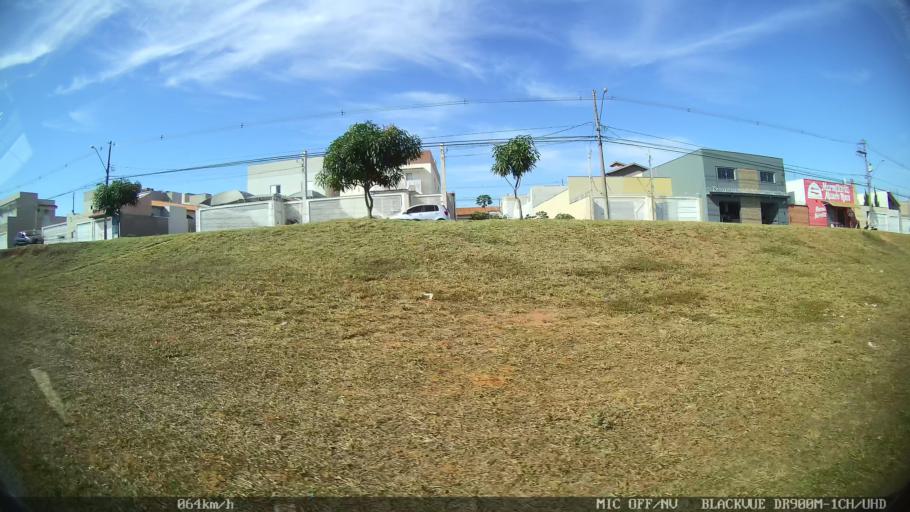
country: BR
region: Sao Paulo
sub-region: Franca
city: Franca
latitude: -20.5114
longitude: -47.4403
